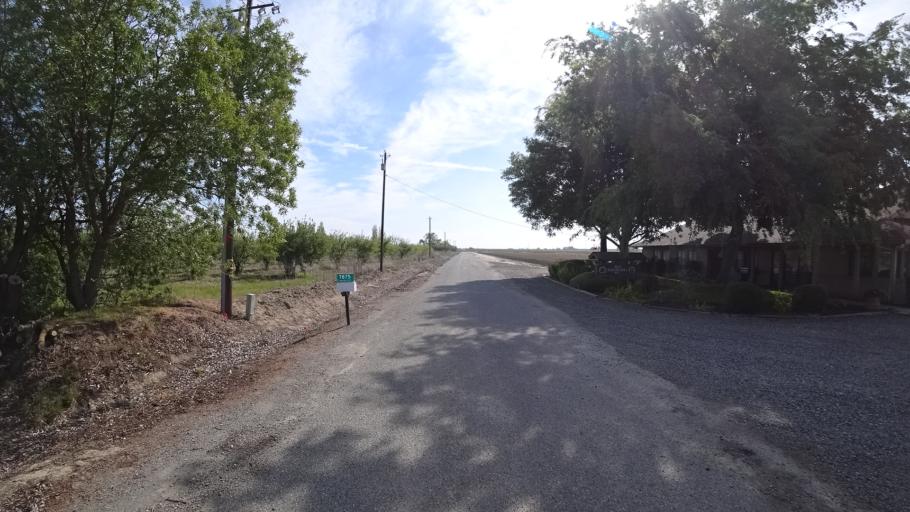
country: US
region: California
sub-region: Glenn County
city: Hamilton City
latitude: 39.6270
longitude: -122.0415
